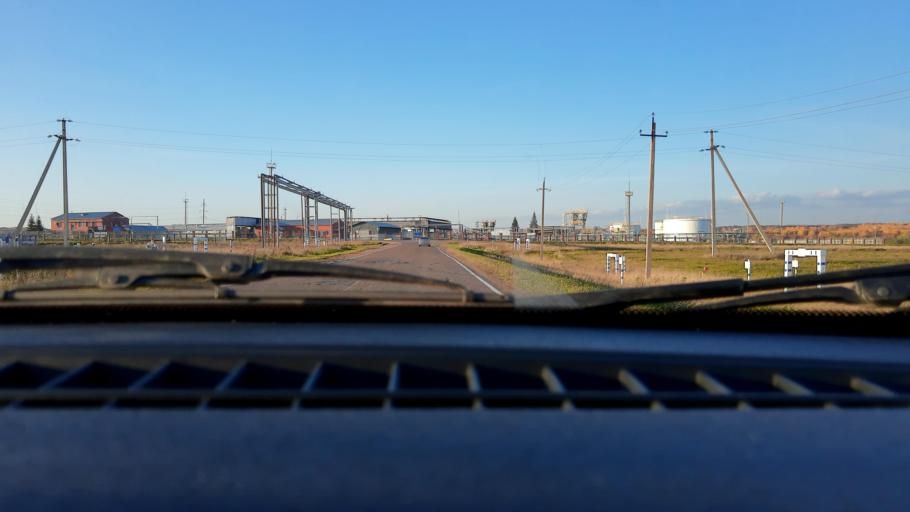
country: RU
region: Bashkortostan
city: Mikhaylovka
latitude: 54.8225
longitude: 55.7654
